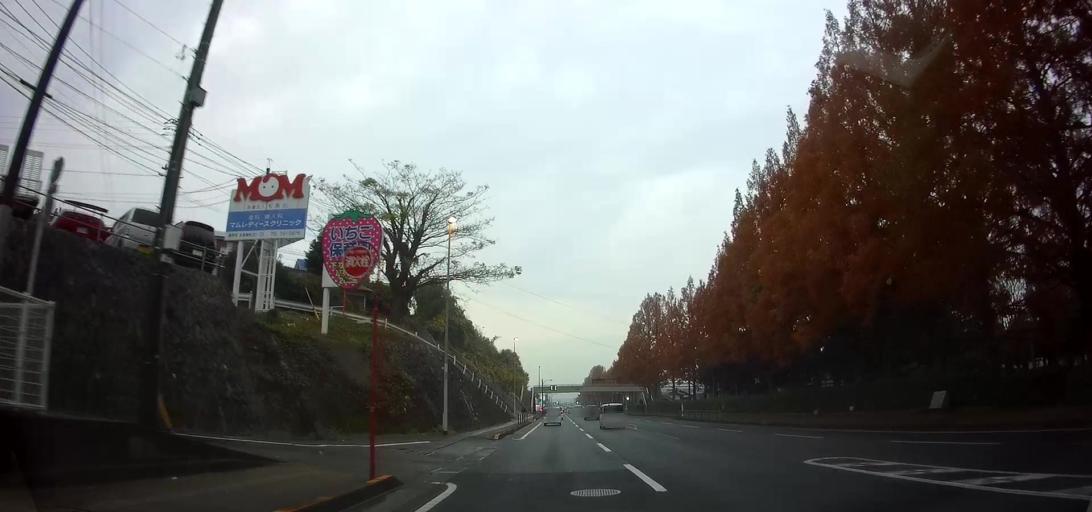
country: JP
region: Nagasaki
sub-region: Isahaya-shi
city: Isahaya
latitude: 32.8360
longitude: 130.0394
